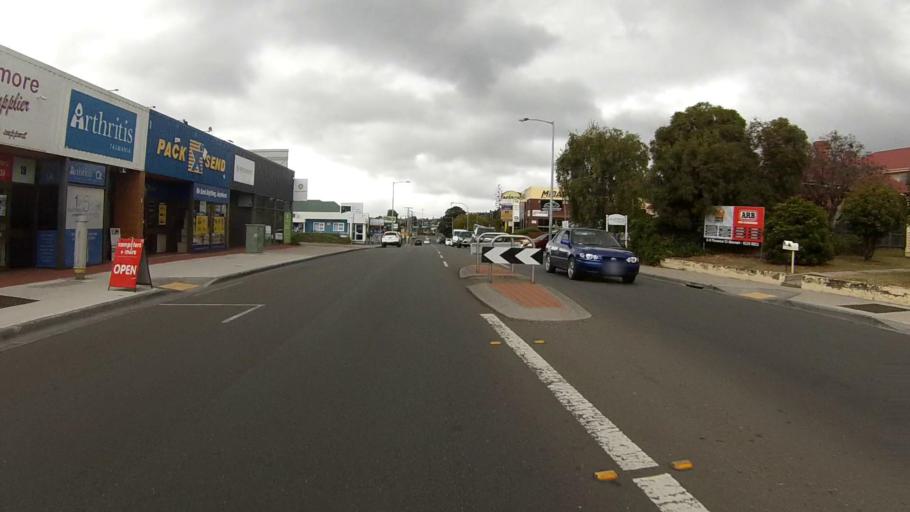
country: AU
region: Tasmania
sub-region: Glenorchy
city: Moonah
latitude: -42.8499
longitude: 147.2974
